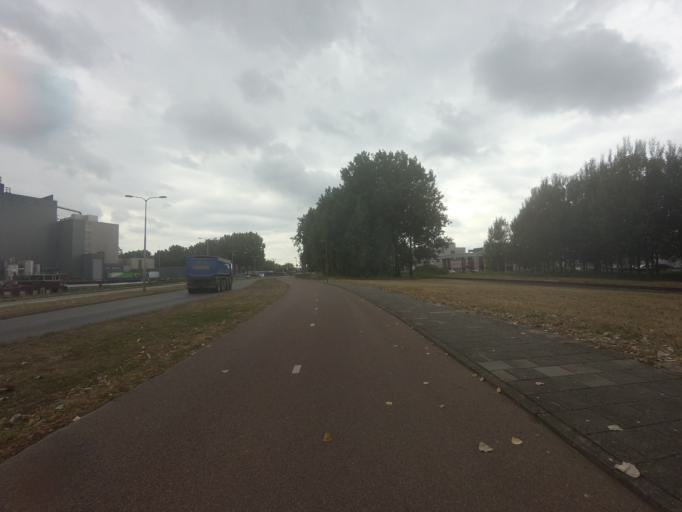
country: NL
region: Utrecht
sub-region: Stichtse Vecht
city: Maarssen
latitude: 52.1175
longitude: 5.0575
